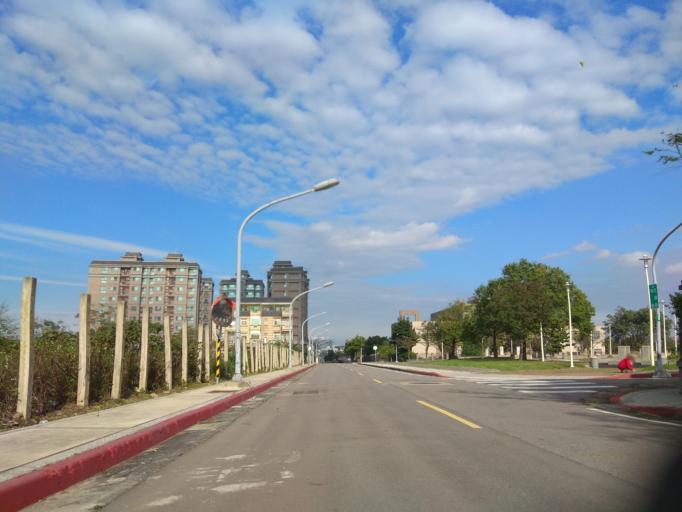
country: TW
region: Taiwan
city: Taoyuan City
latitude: 25.0528
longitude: 121.1772
